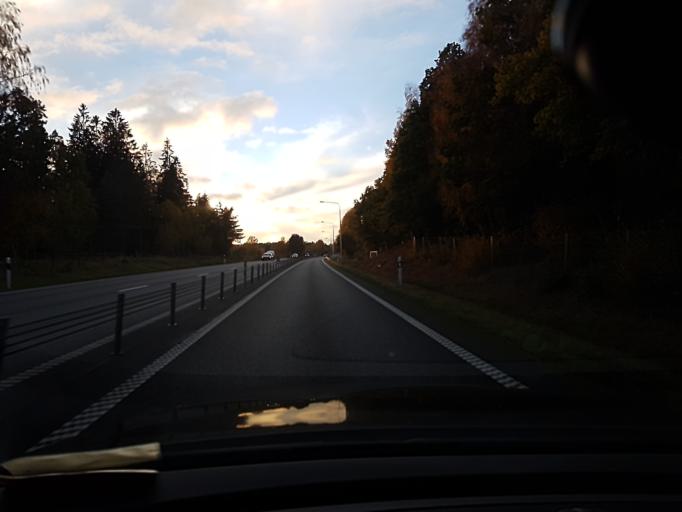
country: SE
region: Kronoberg
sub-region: Ljungby Kommun
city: Lagan
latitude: 56.8519
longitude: 14.0543
